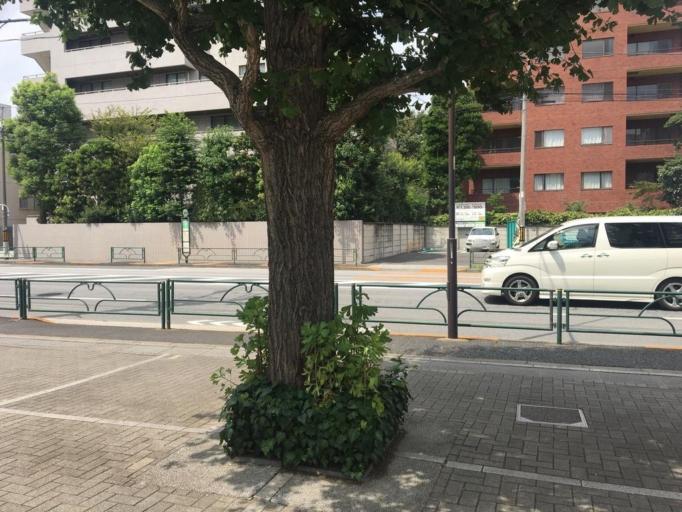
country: JP
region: Tokyo
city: Tokyo
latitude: 35.7307
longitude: 139.7472
